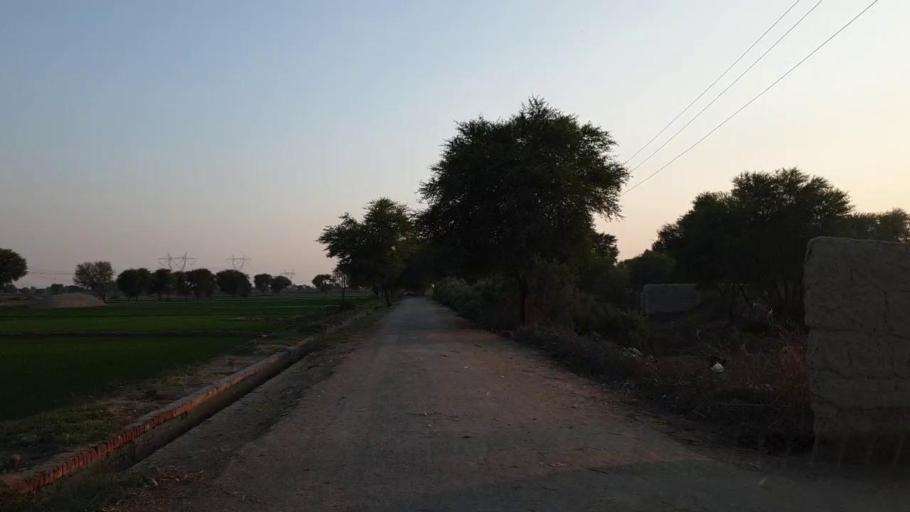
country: PK
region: Sindh
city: Sehwan
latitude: 26.4431
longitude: 67.7618
